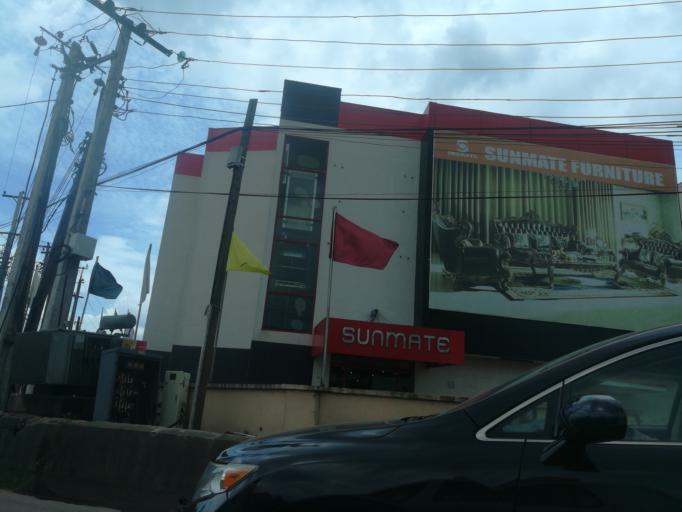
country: NG
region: Lagos
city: Ikeja
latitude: 6.5961
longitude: 3.3548
